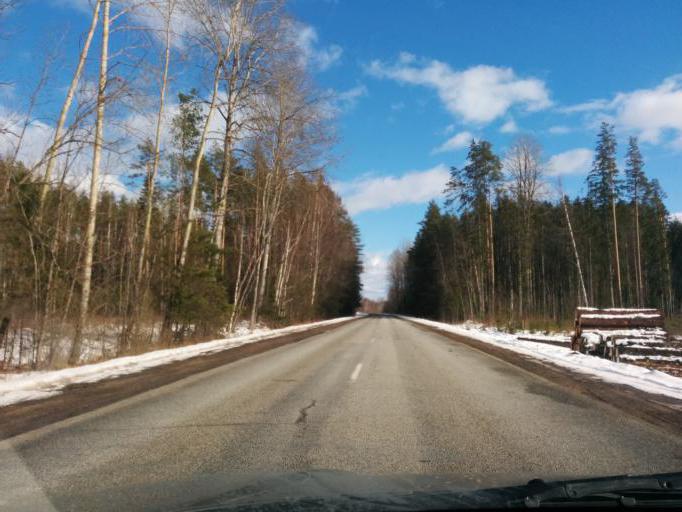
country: LV
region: Gulbenes Rajons
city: Gulbene
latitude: 57.1927
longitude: 26.9679
